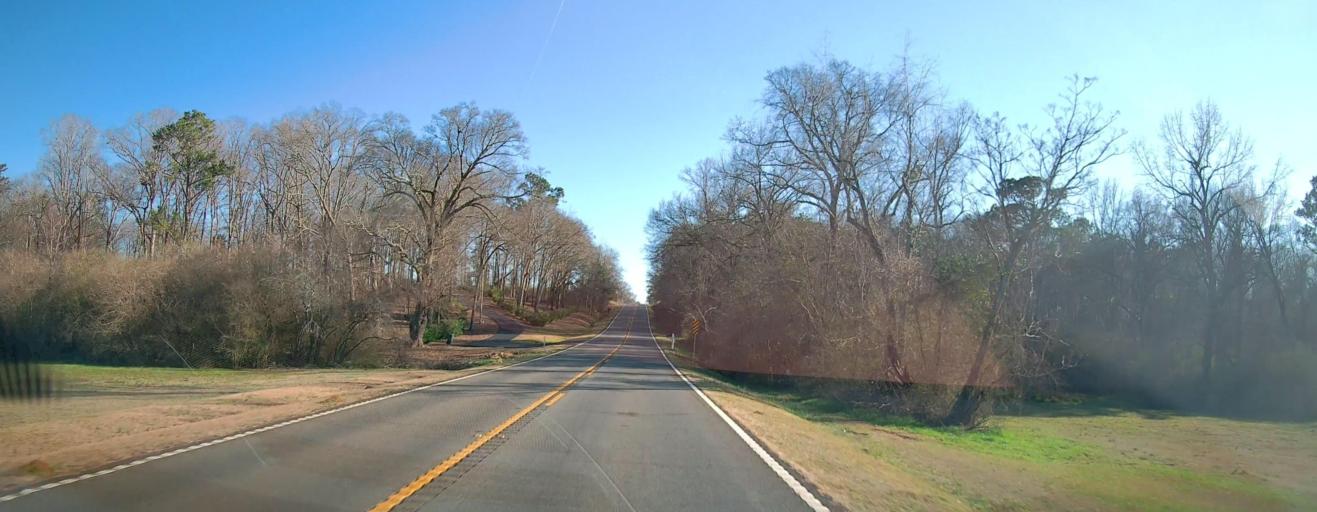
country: US
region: Georgia
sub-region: Sumter County
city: Americus
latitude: 32.0156
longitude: -84.2187
